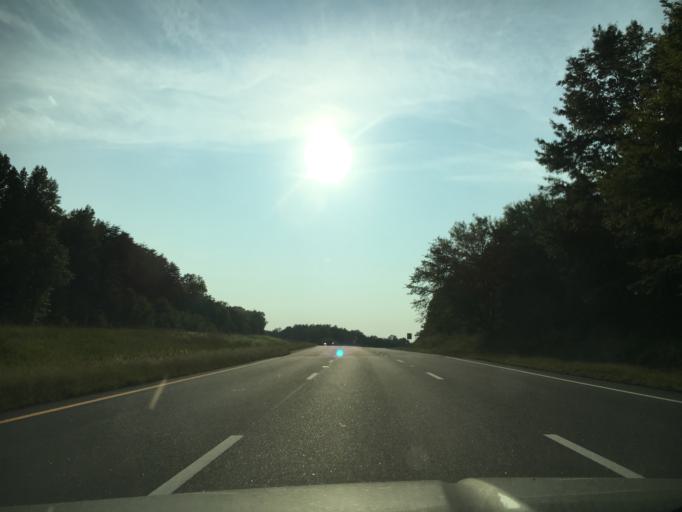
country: US
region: Virginia
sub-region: Prince Edward County
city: Farmville
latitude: 37.2792
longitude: -78.3560
